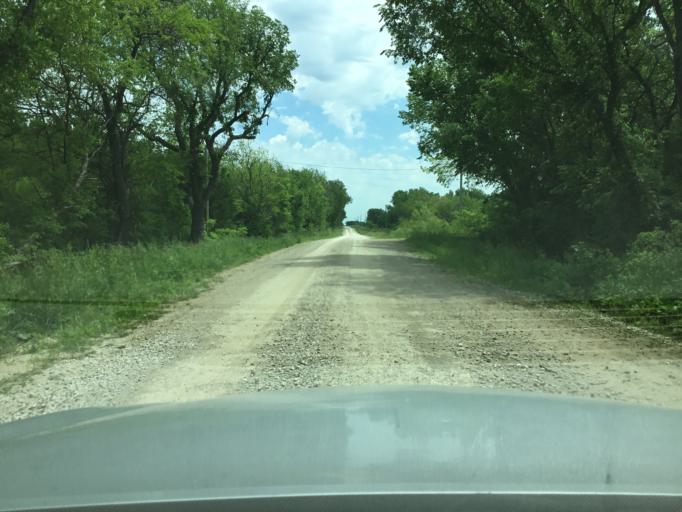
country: US
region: Kansas
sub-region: Montgomery County
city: Independence
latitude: 37.0952
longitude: -95.7926
